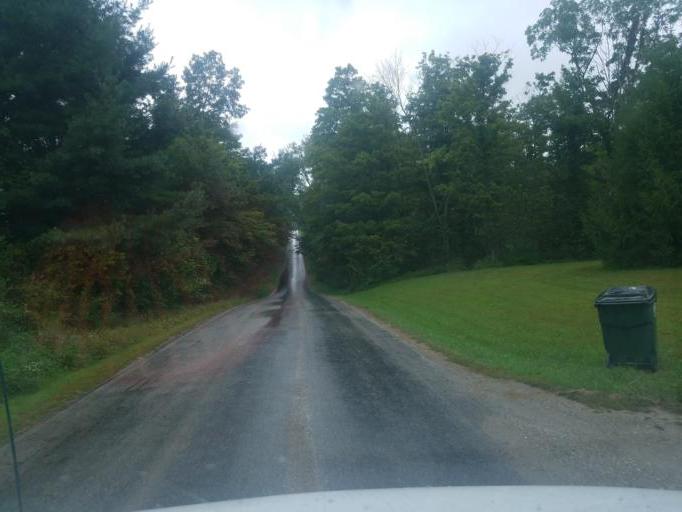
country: US
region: Ohio
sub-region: Wayne County
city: West Salem
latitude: 40.9378
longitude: -82.0365
